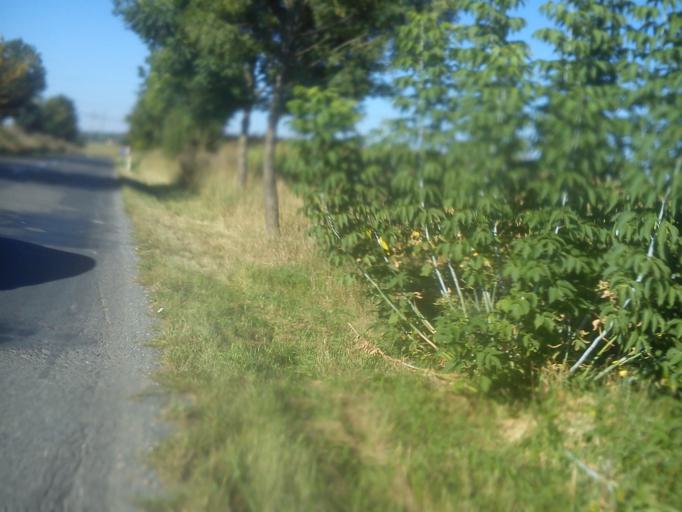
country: CZ
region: South Moravian
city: Telnice
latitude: 49.0954
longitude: 16.7412
